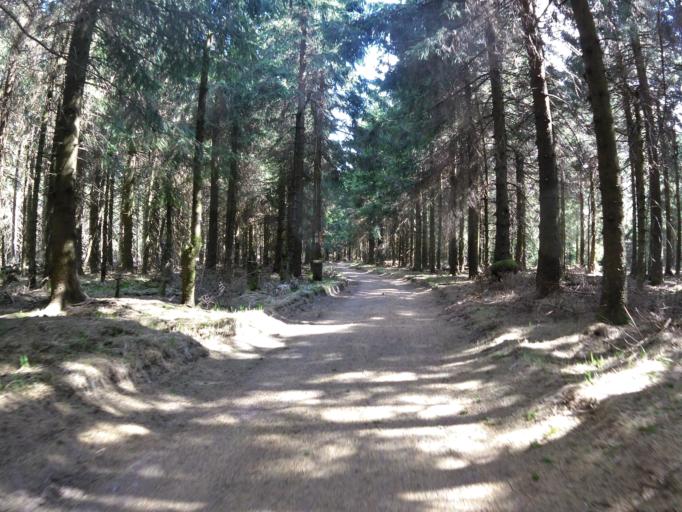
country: DE
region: Thuringia
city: Unterschonau
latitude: 50.7422
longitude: 10.5745
